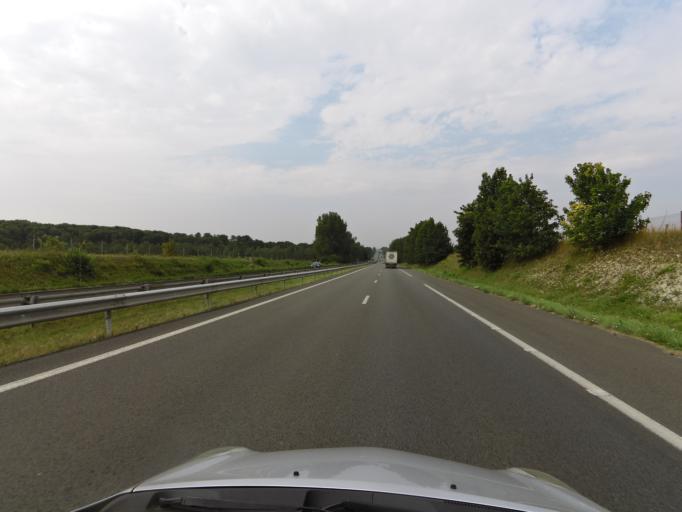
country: FR
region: Nord-Pas-de-Calais
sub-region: Departement du Nord
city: Marcoing
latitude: 50.1080
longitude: 3.1633
